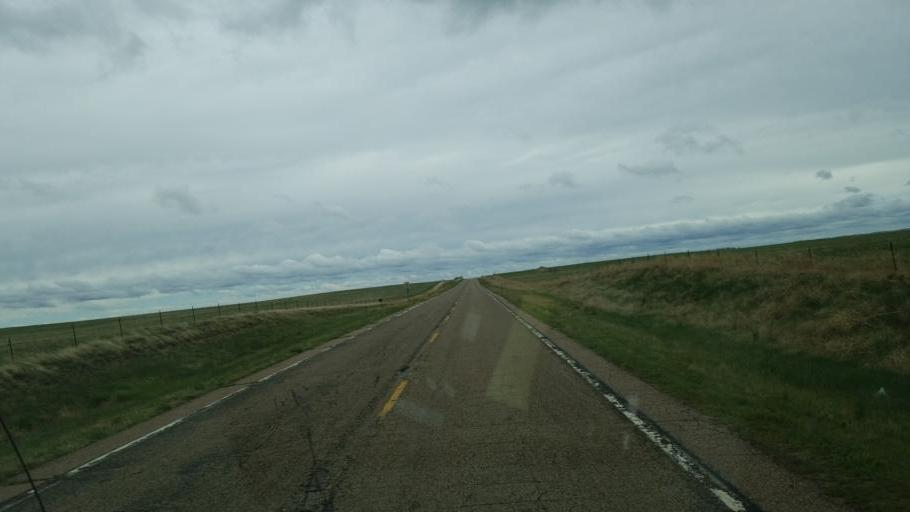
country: US
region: Colorado
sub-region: Lincoln County
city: Hugo
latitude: 38.8521
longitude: -103.7102
